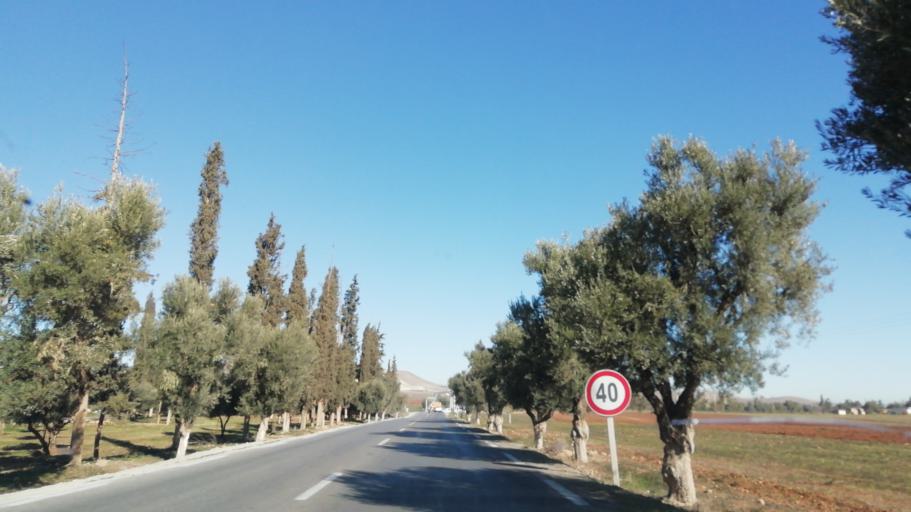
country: DZ
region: Mascara
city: Mascara
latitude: 35.2143
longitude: 0.1117
